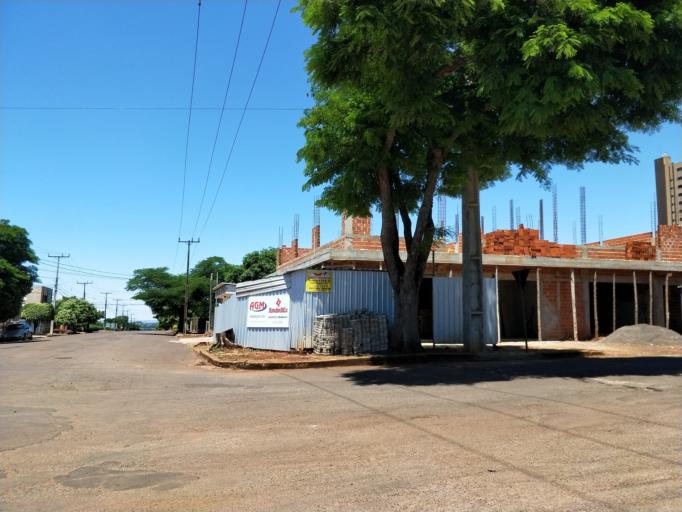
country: BR
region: Parana
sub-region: Marechal Candido Rondon
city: Marechal Candido Rondon
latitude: -24.5665
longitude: -54.0588
